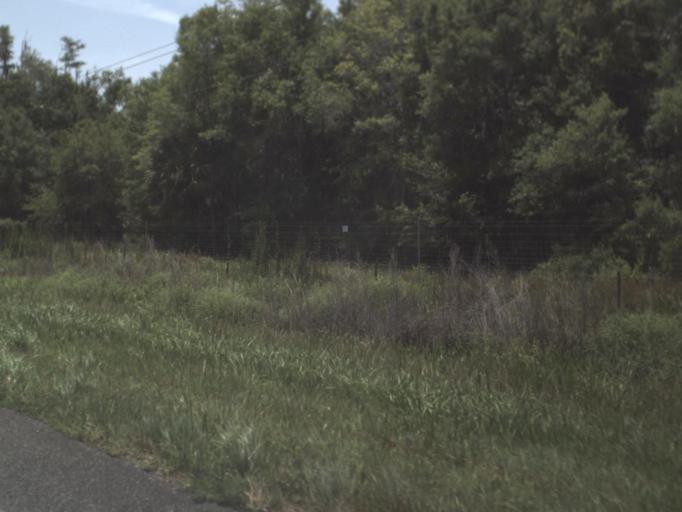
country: US
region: Florida
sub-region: Taylor County
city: Steinhatchee
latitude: 29.8475
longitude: -83.3772
